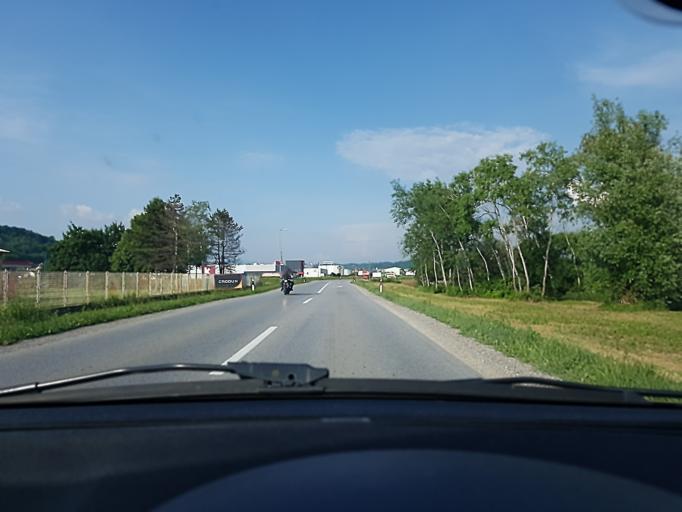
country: HR
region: Krapinsko-Zagorska
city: Zabok
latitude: 46.0161
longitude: 15.8910
